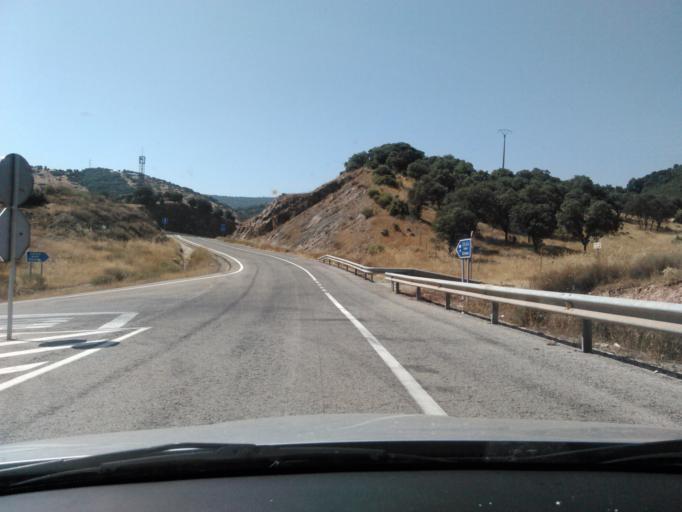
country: ES
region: Andalusia
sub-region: Provincia de Jaen
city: Santa Elena
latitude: 38.4150
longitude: -3.4992
